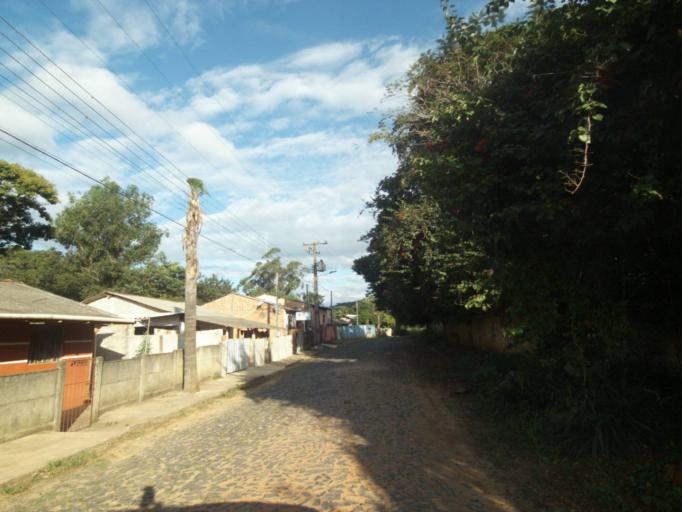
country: BR
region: Parana
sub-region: Telemaco Borba
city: Telemaco Borba
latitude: -24.3223
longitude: -50.6110
